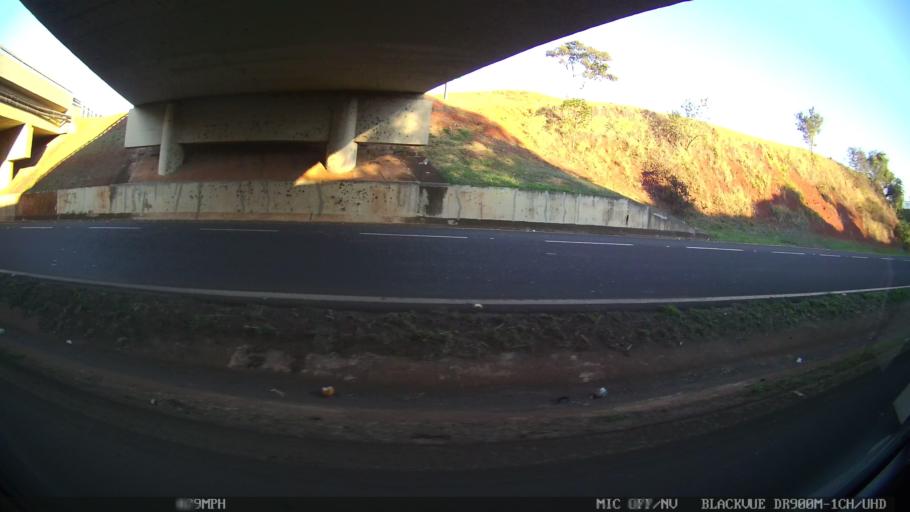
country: BR
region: Sao Paulo
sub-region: Araraquara
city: Araraquara
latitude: -21.7892
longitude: -48.2184
